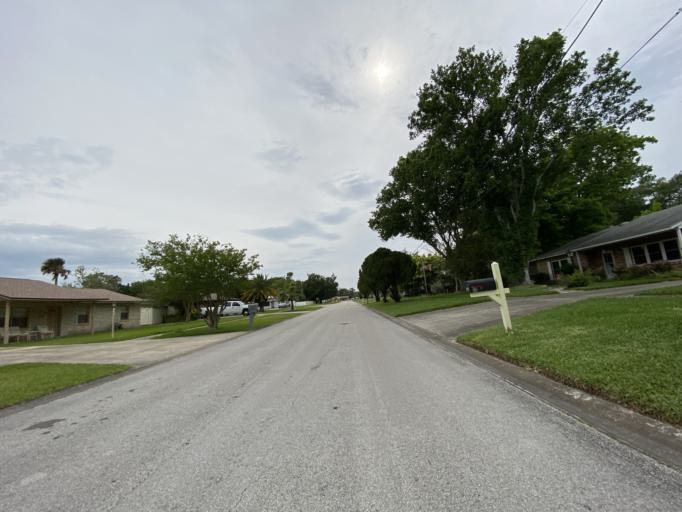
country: US
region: Florida
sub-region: Volusia County
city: South Daytona
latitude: 29.1722
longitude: -81.0175
